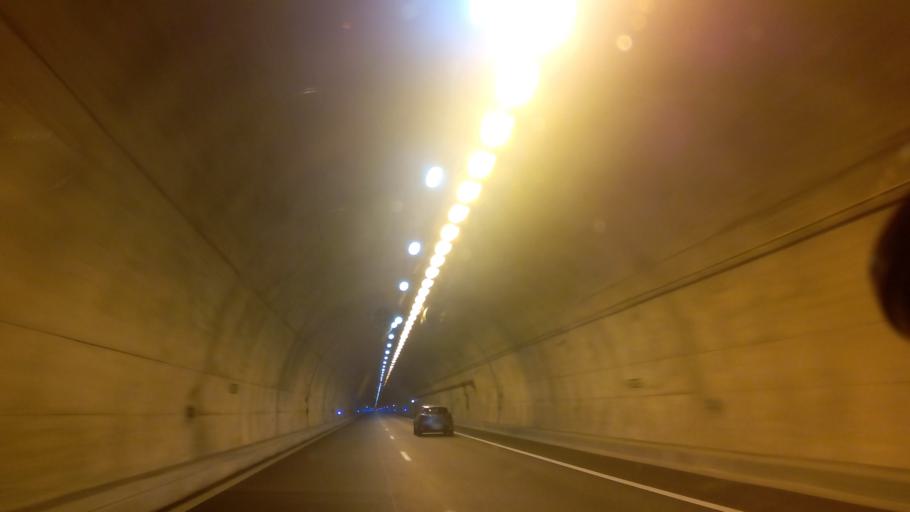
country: PT
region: Vila Real
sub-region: Mesao Frio
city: Mesao Frio
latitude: 41.2682
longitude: -7.9351
